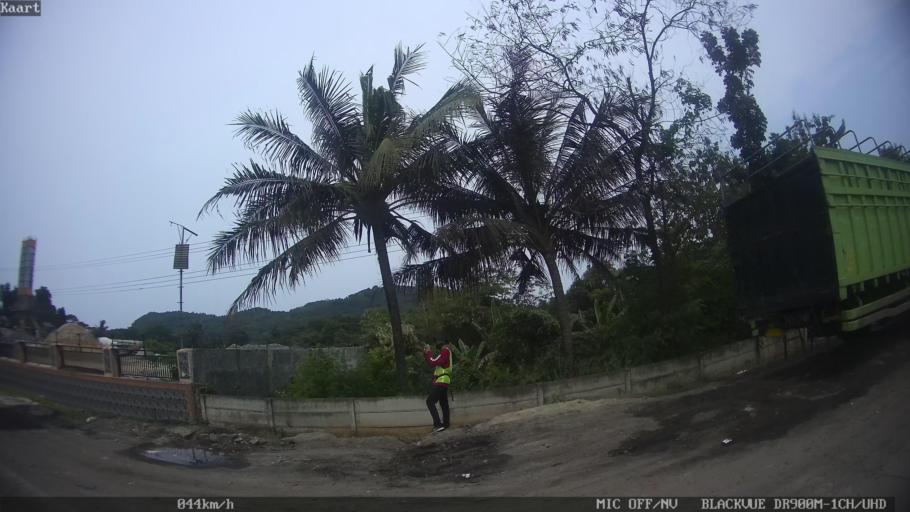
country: ID
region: Lampung
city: Bandarlampung
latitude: -5.4234
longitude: 105.2955
